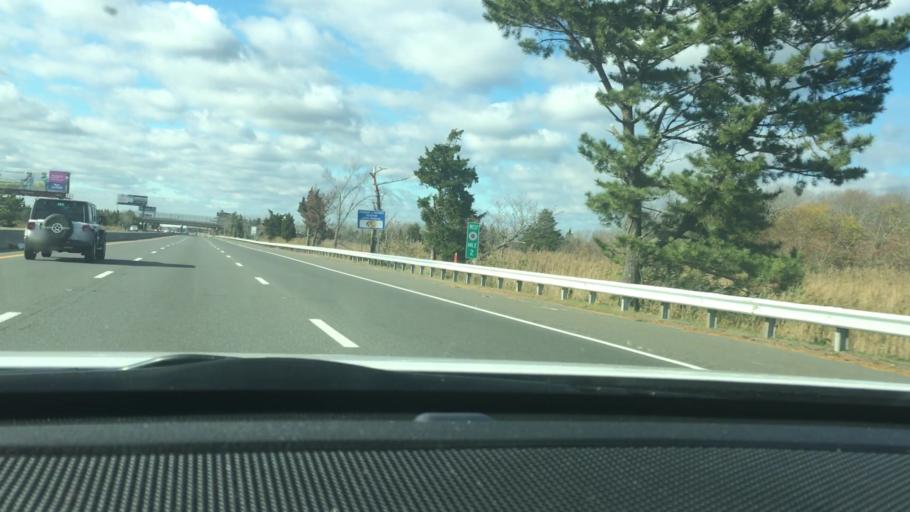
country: US
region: New Jersey
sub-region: Atlantic County
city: Ventnor City
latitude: 39.3737
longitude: -74.4740
